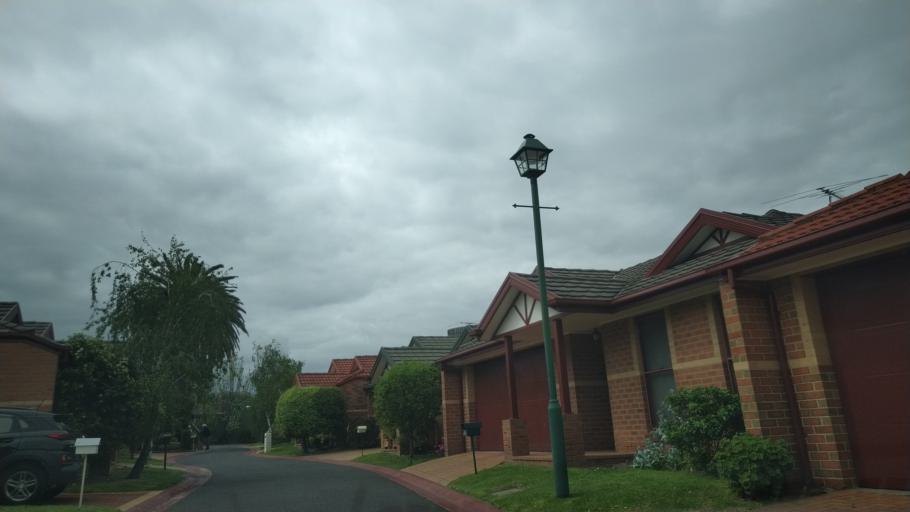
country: AU
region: Victoria
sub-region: Glen Eira
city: Murrumbeena
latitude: -37.8911
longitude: 145.0796
